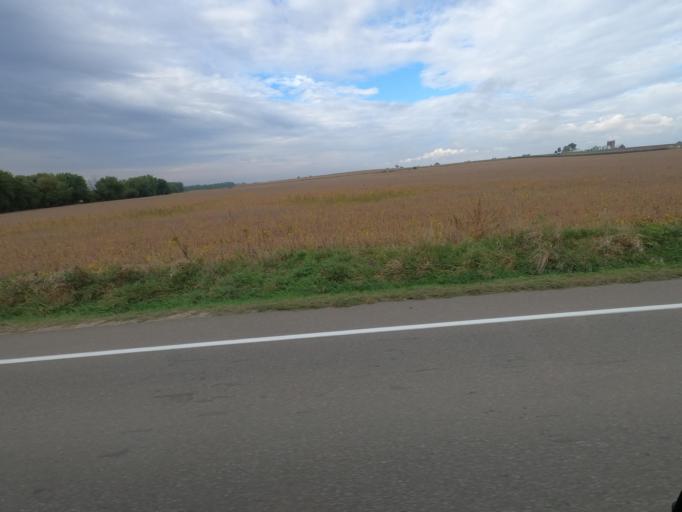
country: US
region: Iowa
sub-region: Henry County
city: Mount Pleasant
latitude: 40.7845
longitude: -91.5700
